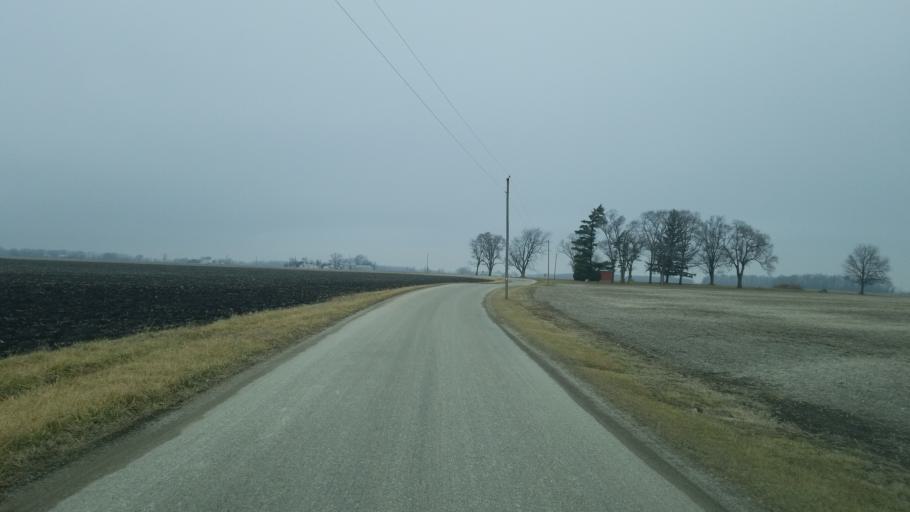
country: US
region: Indiana
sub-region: Adams County
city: Berne
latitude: 40.6758
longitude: -84.8500
